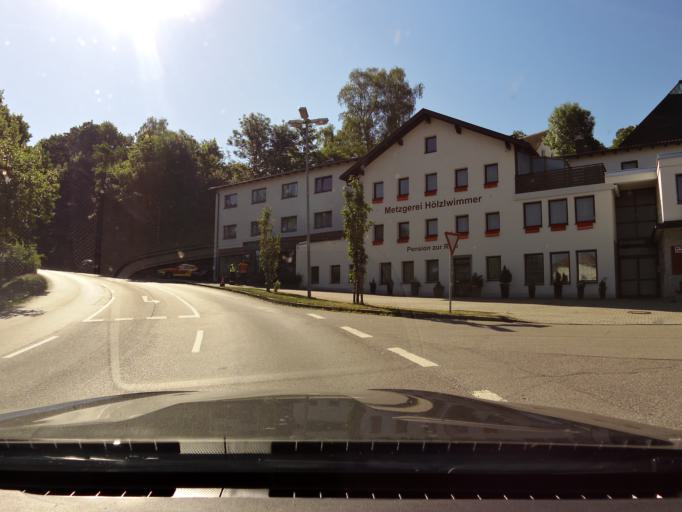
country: DE
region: Bavaria
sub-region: Upper Bavaria
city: Burgkirchen an der Alz
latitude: 48.1666
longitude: 12.7309
